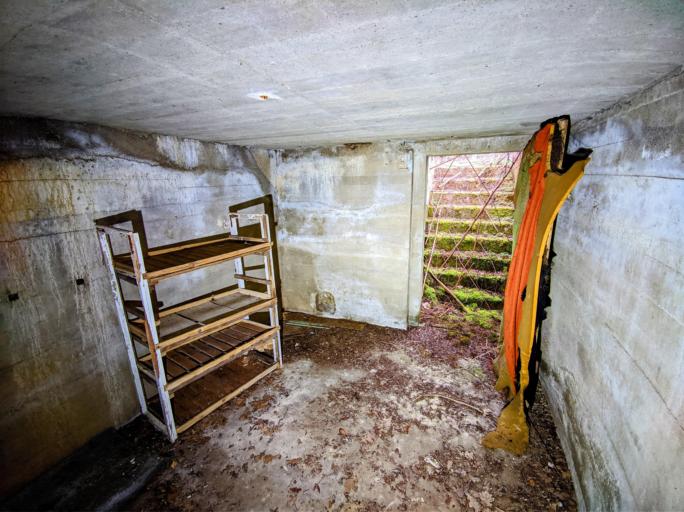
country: PL
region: Lubusz
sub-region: Powiat swiebodzinski
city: Lubrza
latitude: 52.3133
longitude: 15.4222
